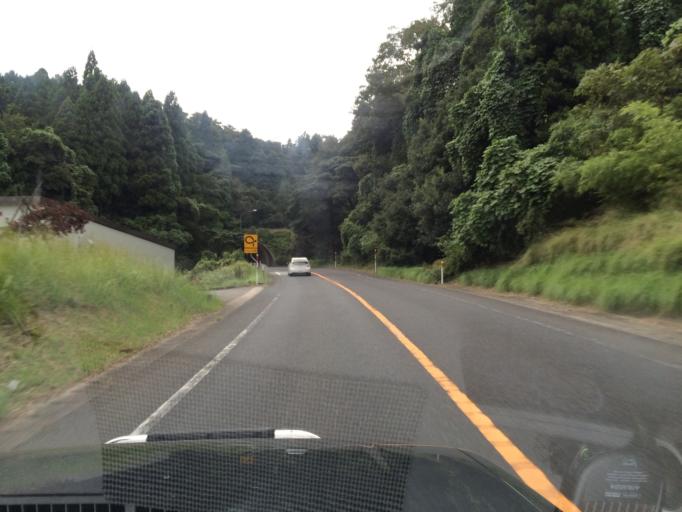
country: JP
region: Hyogo
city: Toyooka
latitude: 35.5129
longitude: 134.7934
